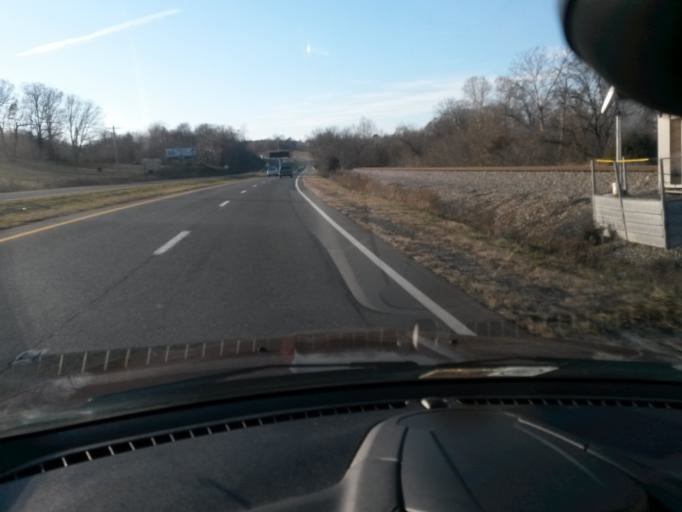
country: US
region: Virginia
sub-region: Amherst County
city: Madison Heights
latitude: 37.3854
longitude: -79.0700
